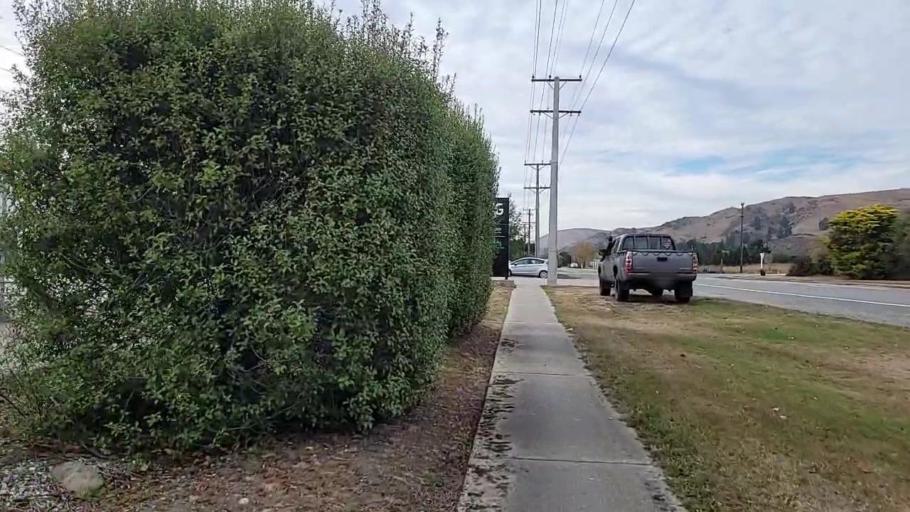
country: NZ
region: Southland
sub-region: Gore District
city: Gore
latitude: -45.6354
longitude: 169.3656
